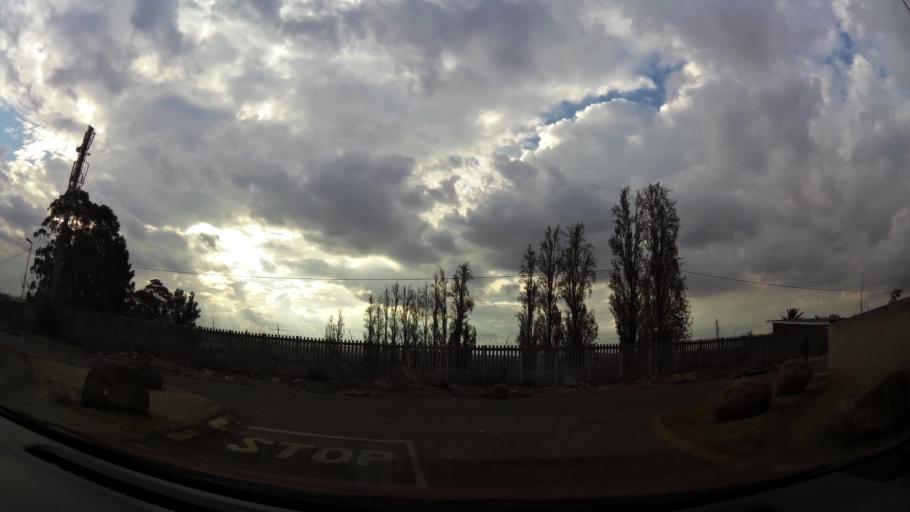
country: ZA
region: Gauteng
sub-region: City of Johannesburg Metropolitan Municipality
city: Soweto
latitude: -26.2411
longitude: 27.8191
